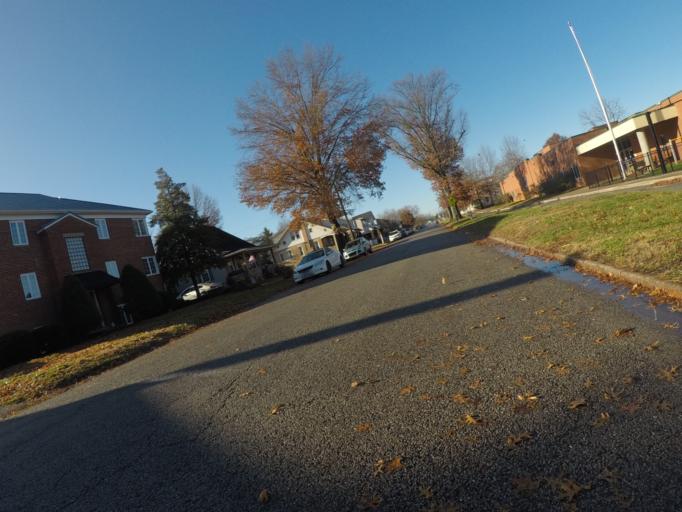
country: US
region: West Virginia
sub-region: Cabell County
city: Huntington
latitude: 38.4104
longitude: -82.4900
